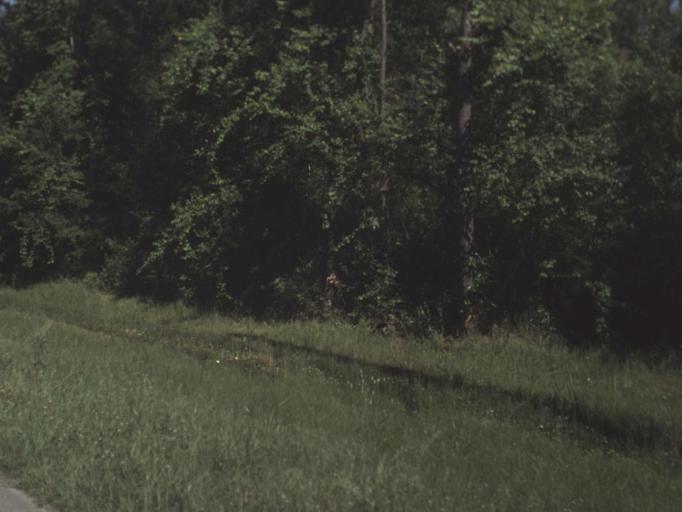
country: US
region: Florida
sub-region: Duval County
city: Baldwin
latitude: 30.3029
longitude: -81.9591
